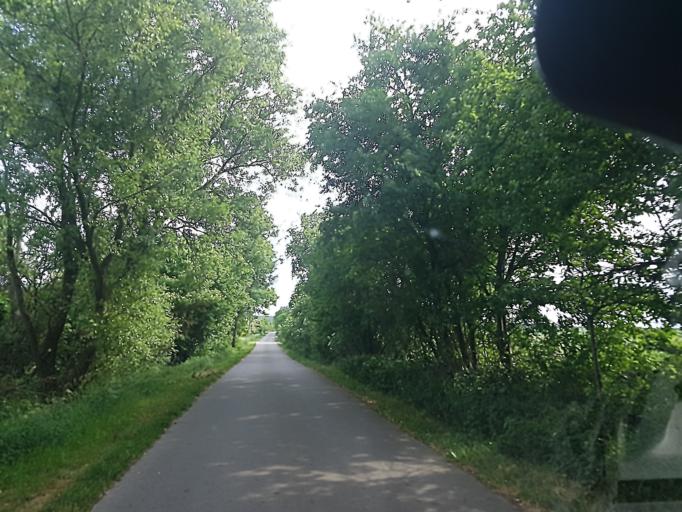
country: DE
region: Brandenburg
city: Niemegk
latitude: 52.0167
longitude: 12.6629
